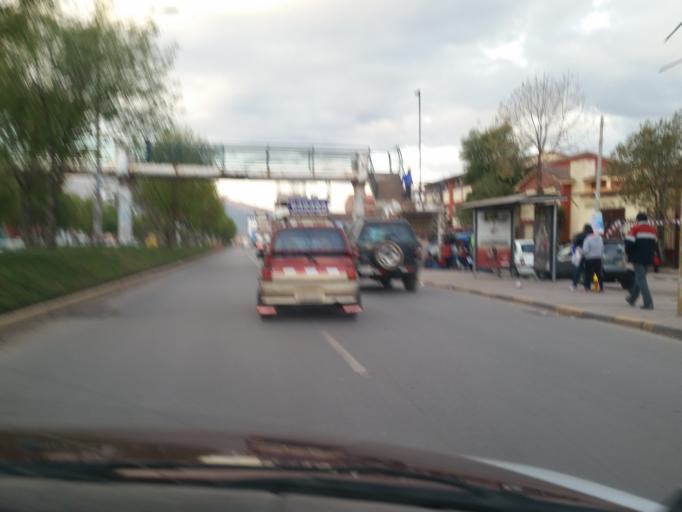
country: PE
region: Cusco
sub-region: Provincia de Cusco
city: Cusco
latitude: -13.5327
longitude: -71.9604
